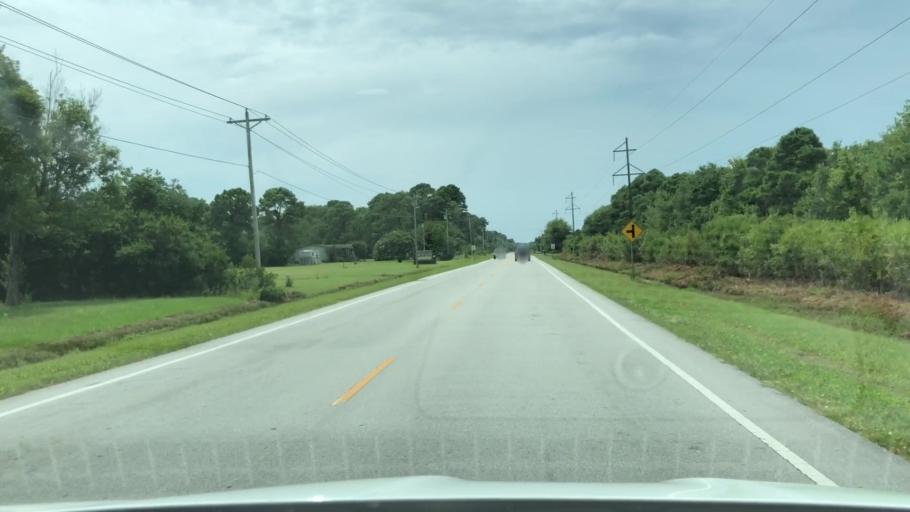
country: US
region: North Carolina
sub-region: Carteret County
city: Newport
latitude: 34.7476
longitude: -76.8798
